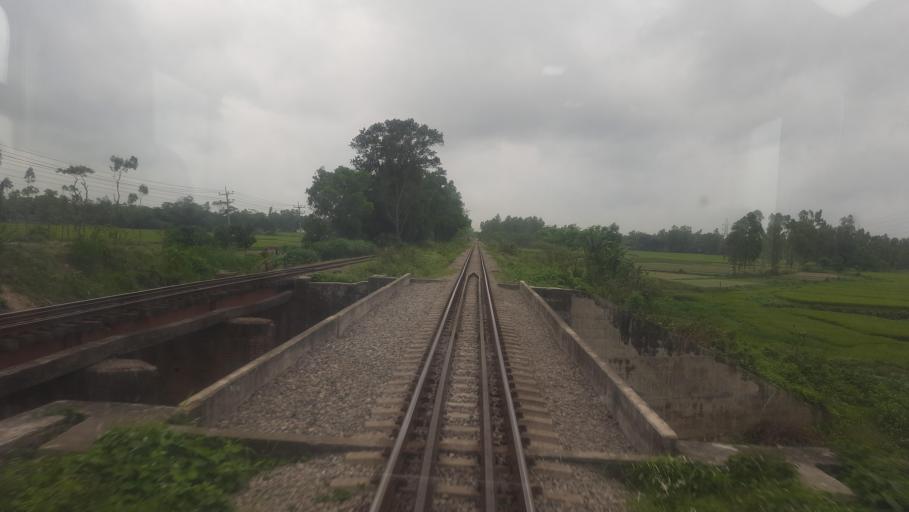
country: BD
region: Dhaka
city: Narsingdi
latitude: 23.9447
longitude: 90.7865
